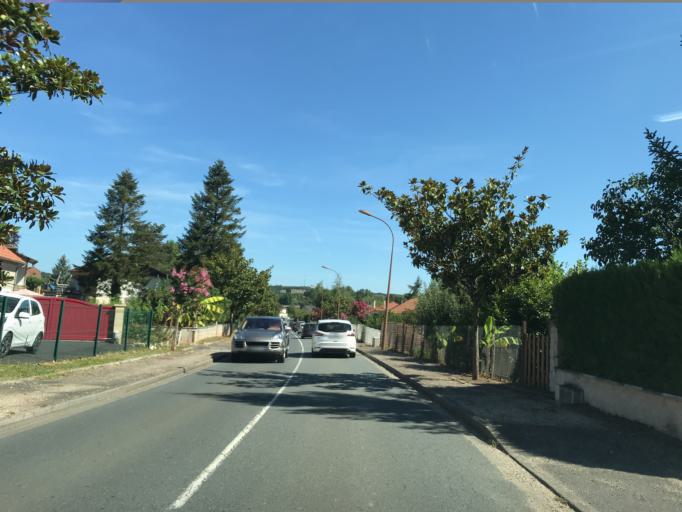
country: FR
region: Limousin
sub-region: Departement de la Correze
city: Larche
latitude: 45.1198
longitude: 1.4107
